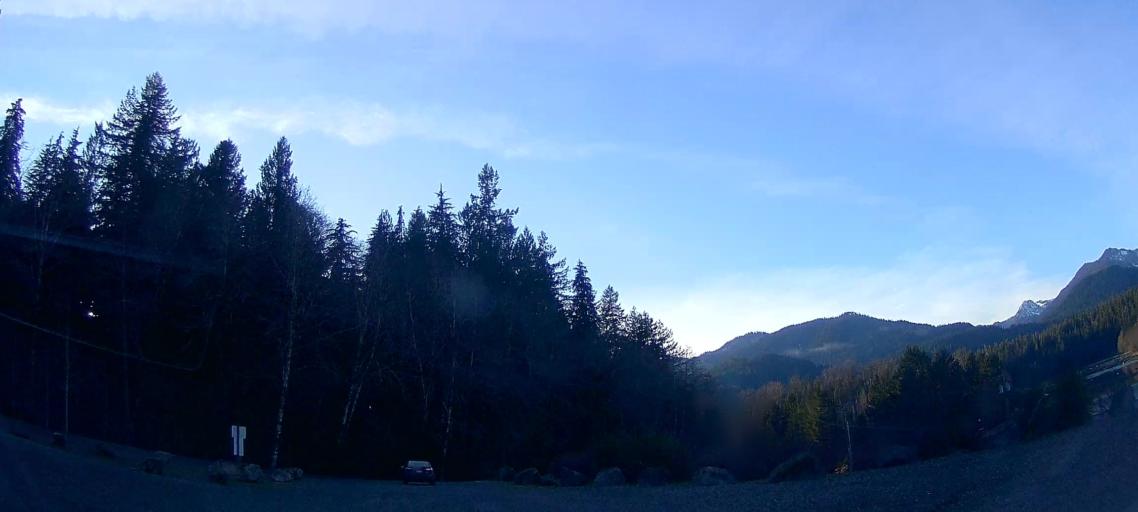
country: US
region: Washington
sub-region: Snohomish County
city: Darrington
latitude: 48.6563
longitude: -121.6869
